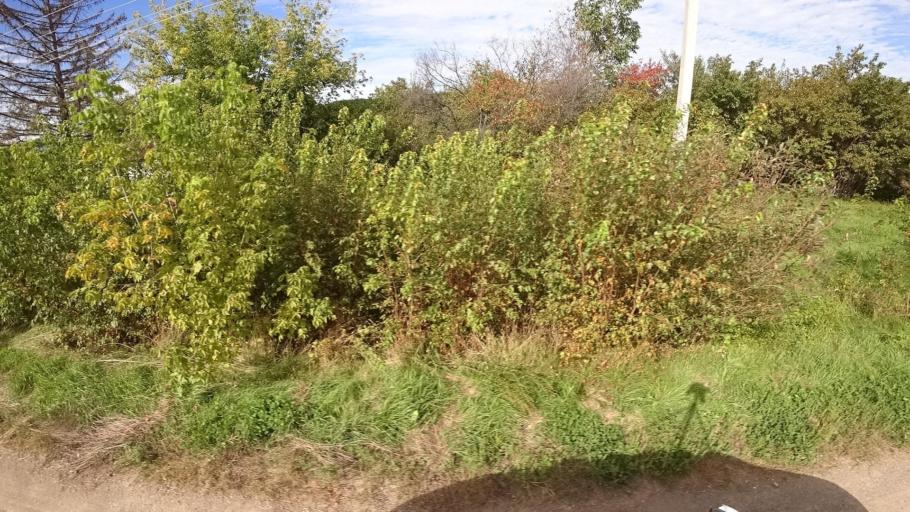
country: RU
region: Primorskiy
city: Dostoyevka
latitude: 44.3274
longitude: 133.4953
